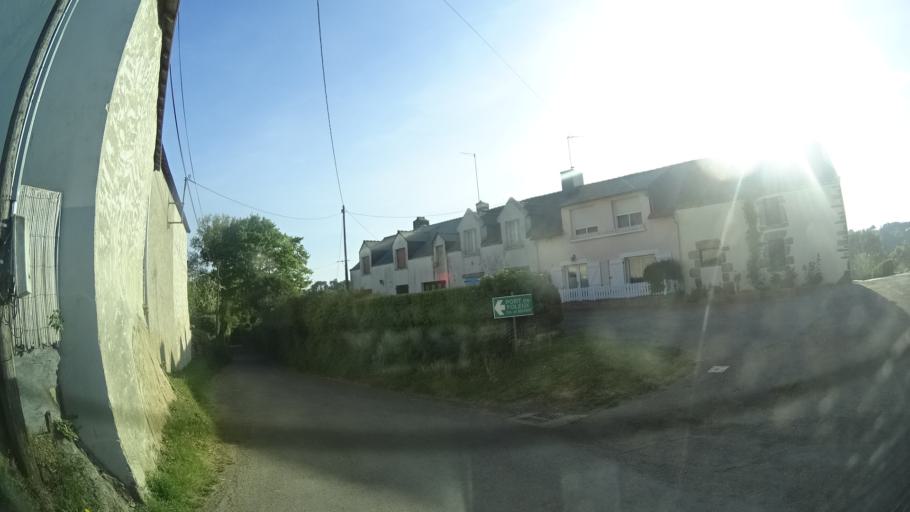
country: FR
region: Brittany
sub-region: Departement du Morbihan
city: Nivillac
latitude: 47.5792
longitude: -2.2838
